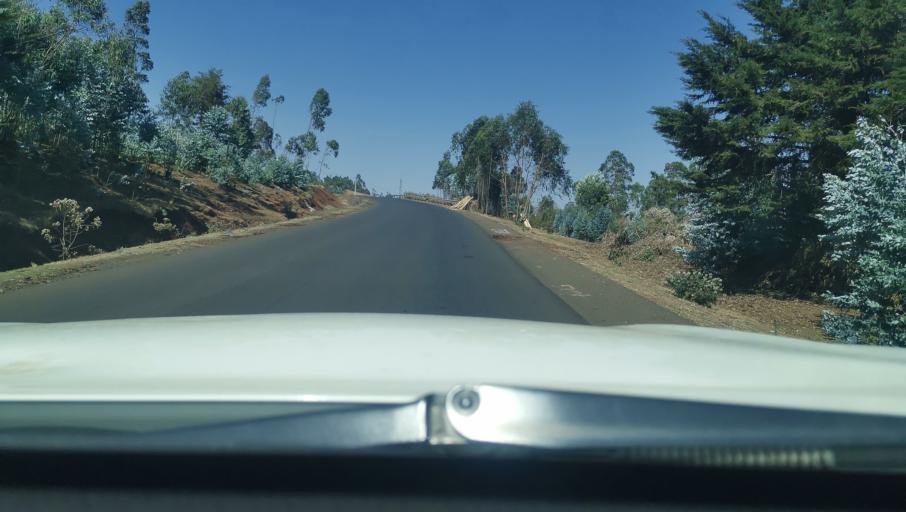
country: ET
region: Oromiya
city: Gedo
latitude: 8.9801
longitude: 37.4760
